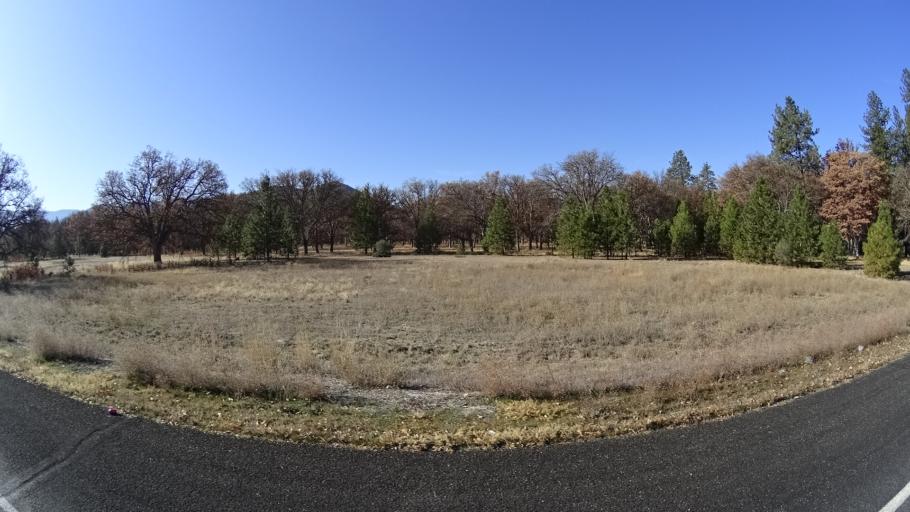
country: US
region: California
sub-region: Siskiyou County
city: Yreka
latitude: 41.6941
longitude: -122.6411
